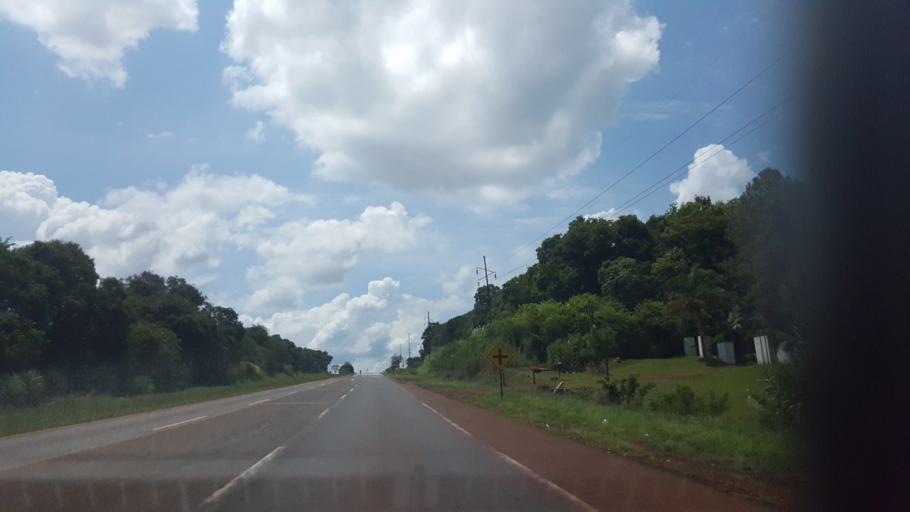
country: AR
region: Misiones
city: Puerto Rico
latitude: -26.8280
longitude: -55.0320
